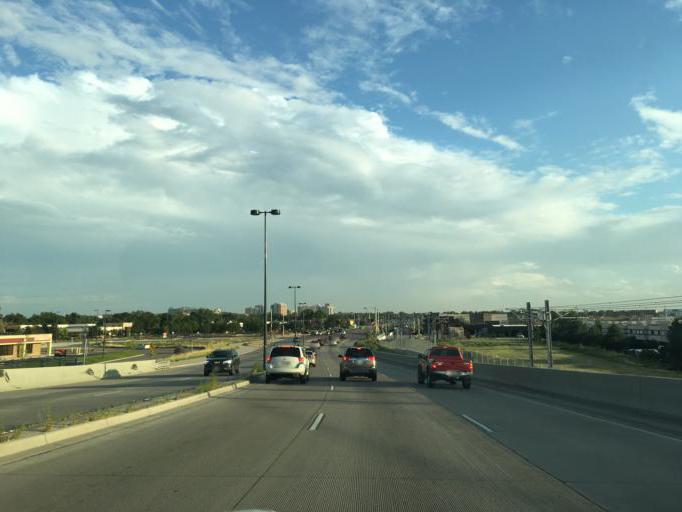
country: US
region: Colorado
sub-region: Adams County
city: Aurora
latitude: 39.7662
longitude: -104.8475
